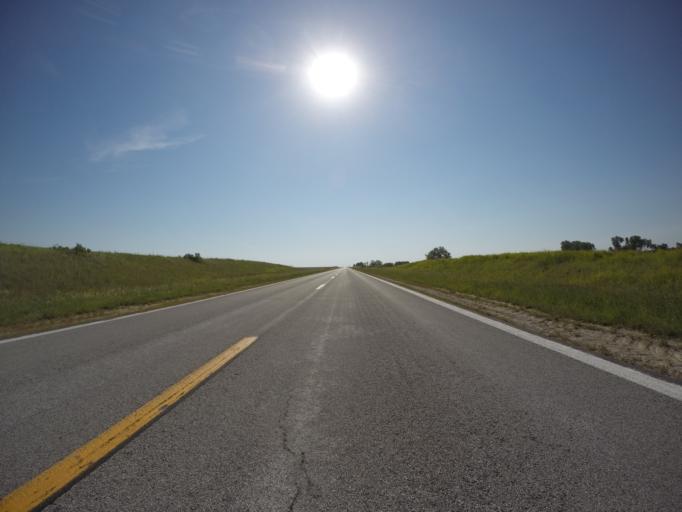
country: US
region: Nebraska
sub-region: Pawnee County
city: Pawnee City
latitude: 40.0447
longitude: -96.3616
